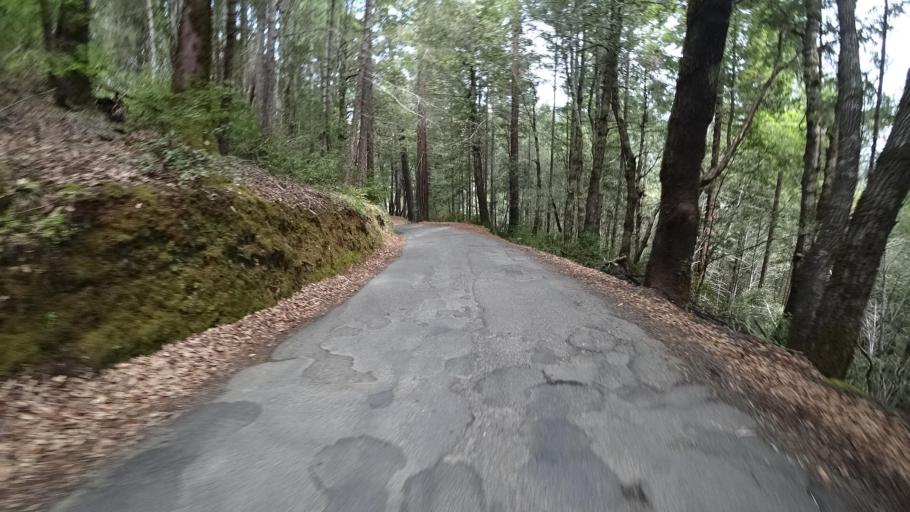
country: US
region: California
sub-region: Humboldt County
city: Redway
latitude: 40.0654
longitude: -123.8298
